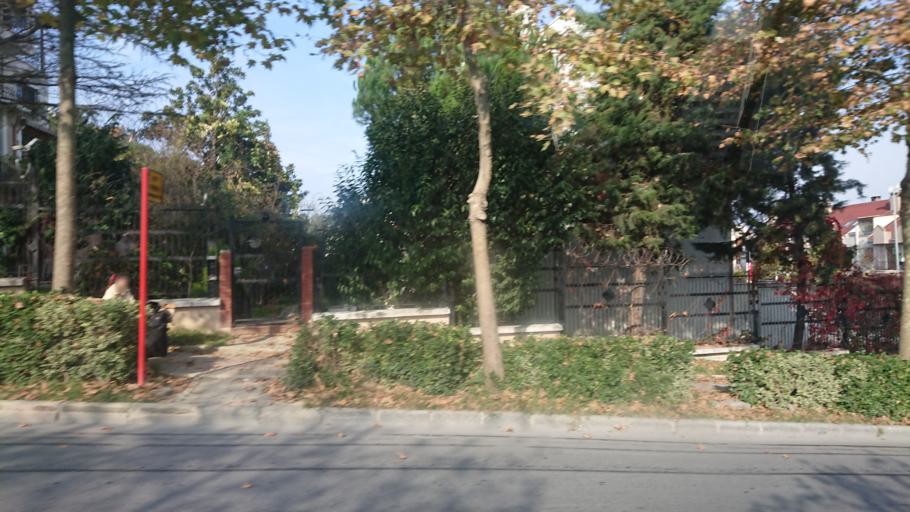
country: TR
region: Istanbul
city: Esenyurt
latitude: 41.0785
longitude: 28.6747
